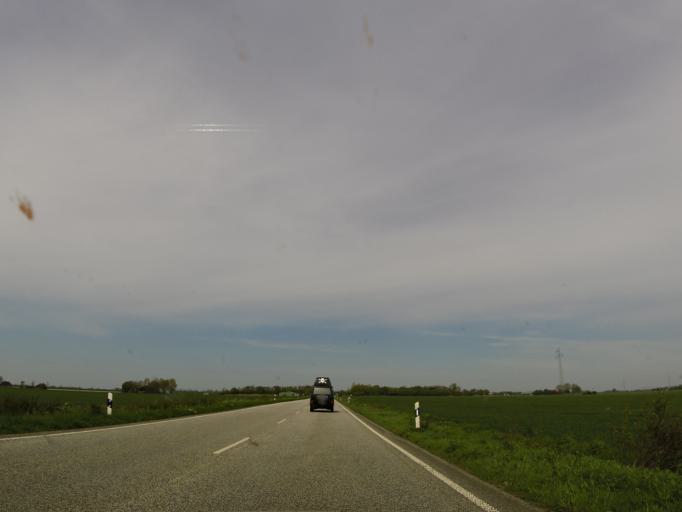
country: DE
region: Schleswig-Holstein
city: Groven
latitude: 54.2939
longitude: 8.9765
